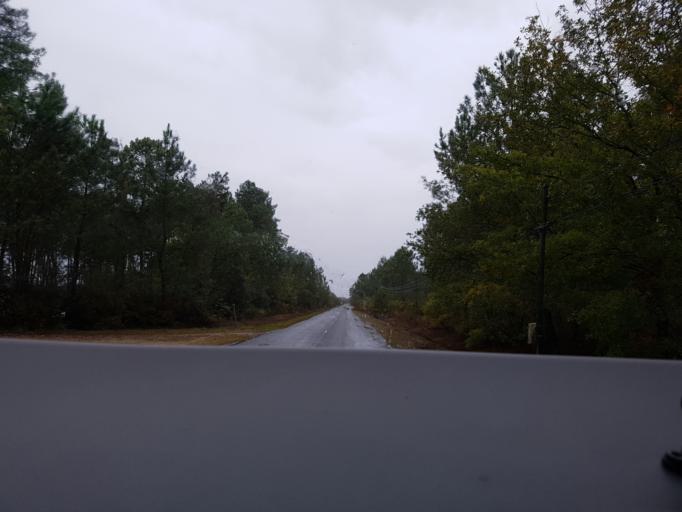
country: FR
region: Aquitaine
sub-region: Departement de la Gironde
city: Saint-Symphorien
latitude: 44.3508
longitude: -0.6202
